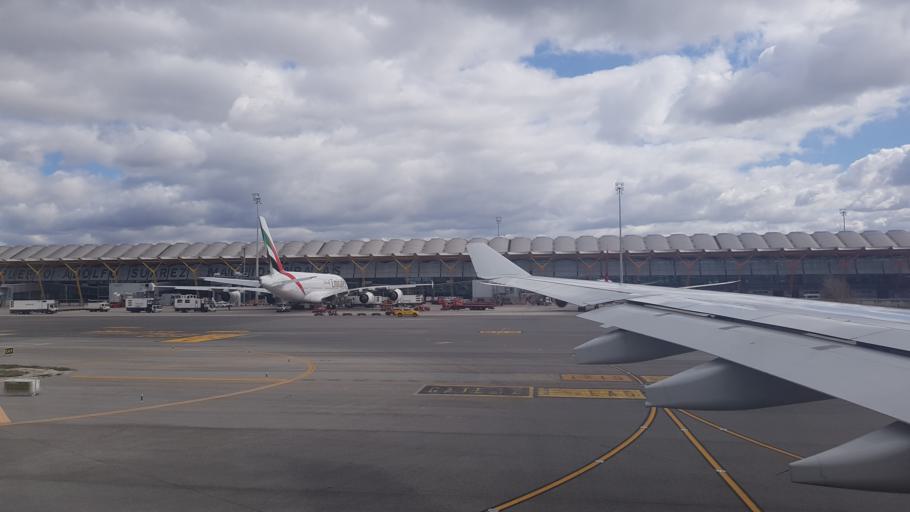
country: ES
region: Madrid
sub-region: Provincia de Madrid
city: Barajas de Madrid
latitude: 40.4929
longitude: -3.5711
